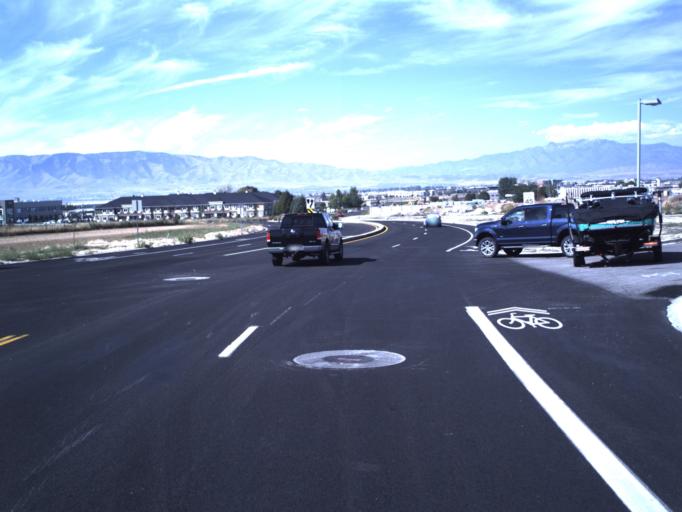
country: US
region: Utah
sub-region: Utah County
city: Pleasant Grove
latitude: 40.3515
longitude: -111.7330
